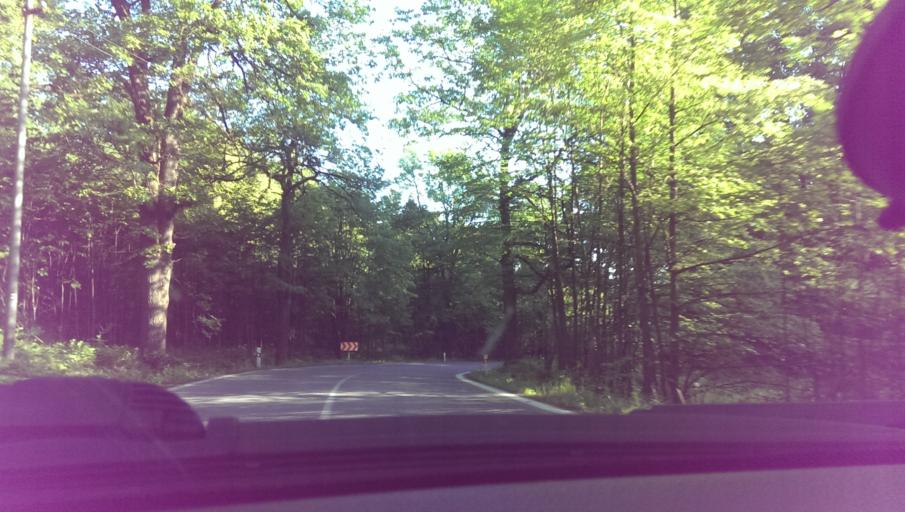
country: CZ
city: Kuncice pod Ondrejnikem
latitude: 49.5473
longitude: 18.2425
